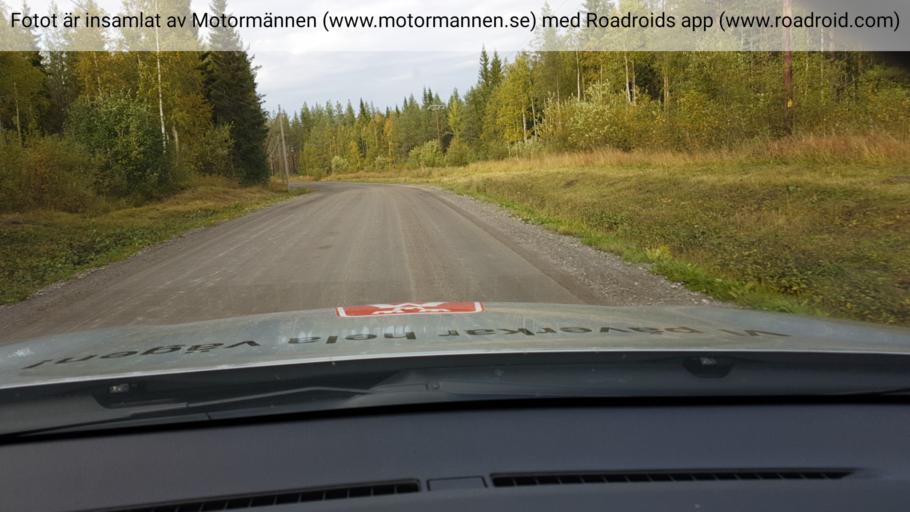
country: SE
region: Jaemtland
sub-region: Stroemsunds Kommun
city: Stroemsund
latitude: 63.9774
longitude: 15.8227
